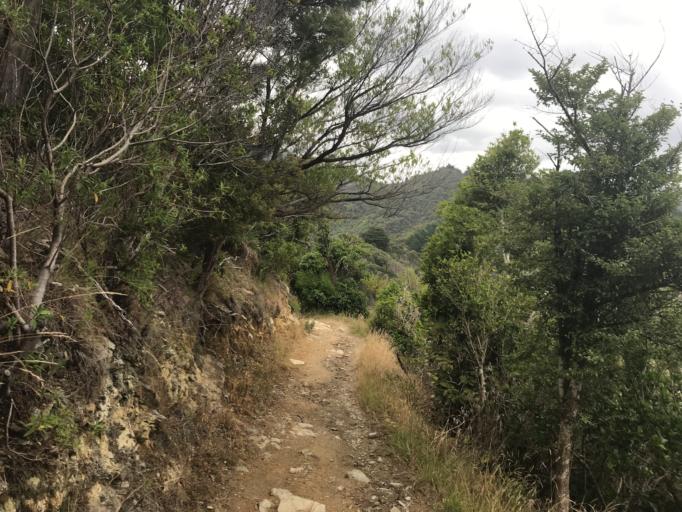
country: NZ
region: Marlborough
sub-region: Marlborough District
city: Picton
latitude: -41.2181
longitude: 173.9748
